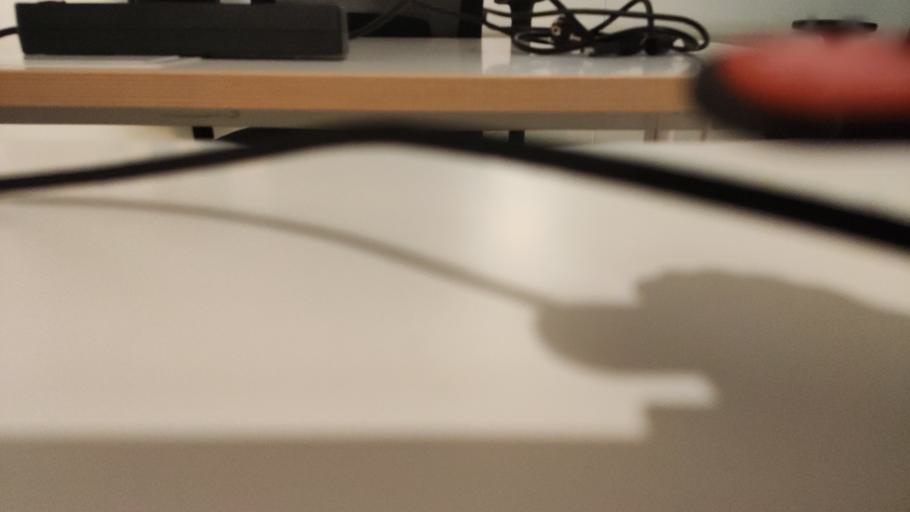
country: RU
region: Moskovskaya
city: Obolensk
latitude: 54.9878
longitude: 37.3082
